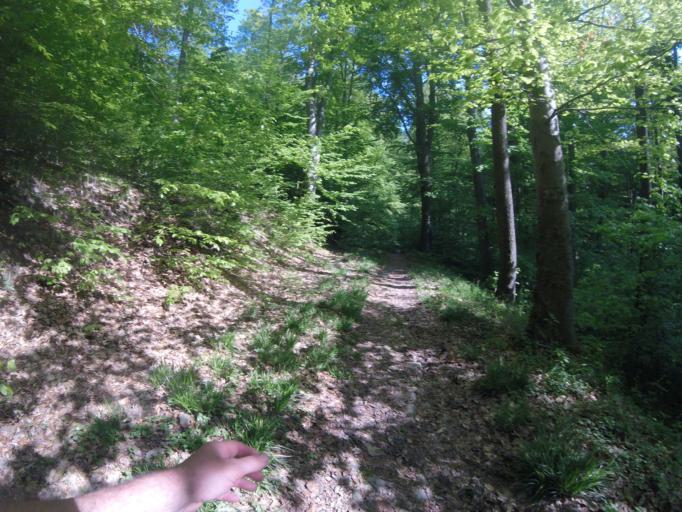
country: HU
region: Pest
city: Pilisszentkereszt
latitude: 47.7076
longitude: 18.8983
